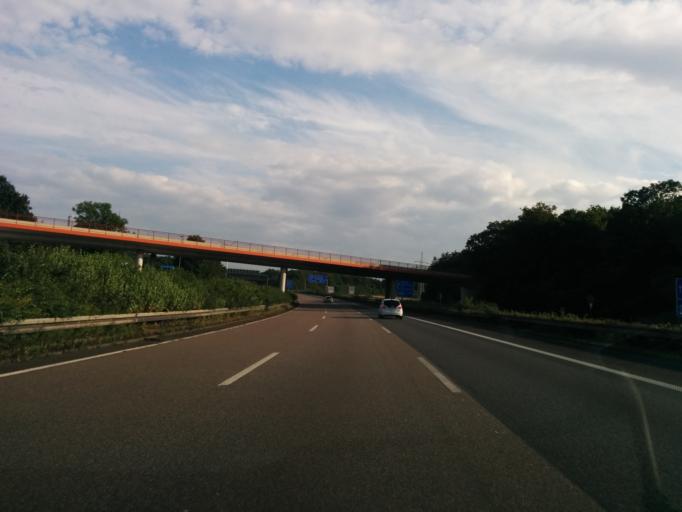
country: DE
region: Hesse
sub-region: Regierungsbezirk Kassel
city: Lohfelden
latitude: 51.2667
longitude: 9.5167
